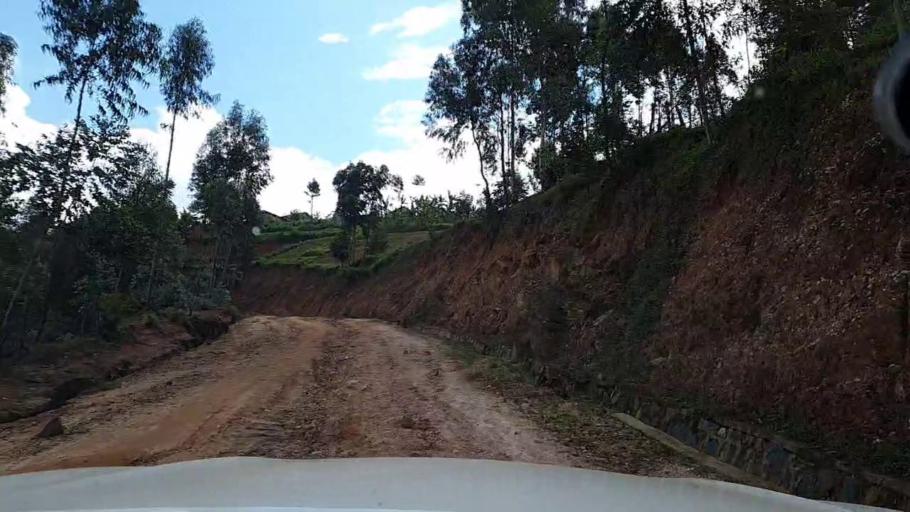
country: RW
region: Southern Province
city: Nzega
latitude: -2.7022
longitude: 29.4337
